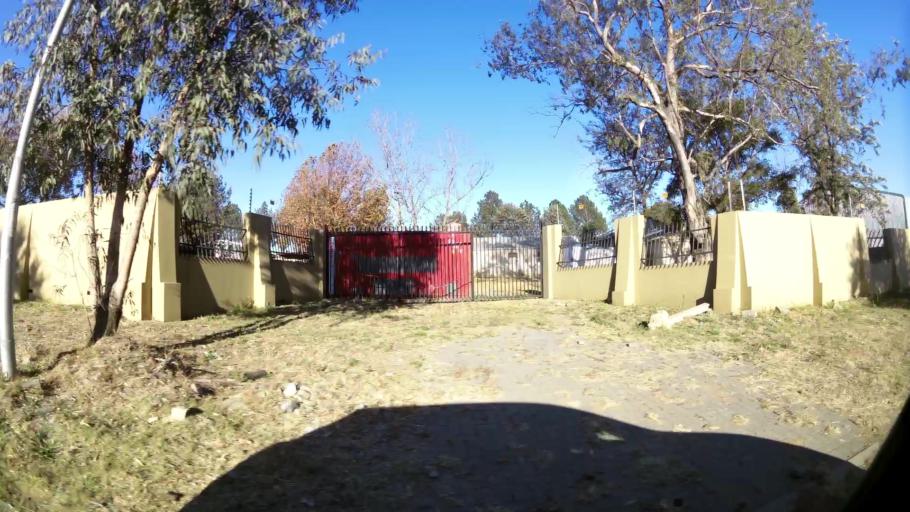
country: ZA
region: Gauteng
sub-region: City of Johannesburg Metropolitan Municipality
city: Midrand
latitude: -26.0334
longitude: 28.1412
